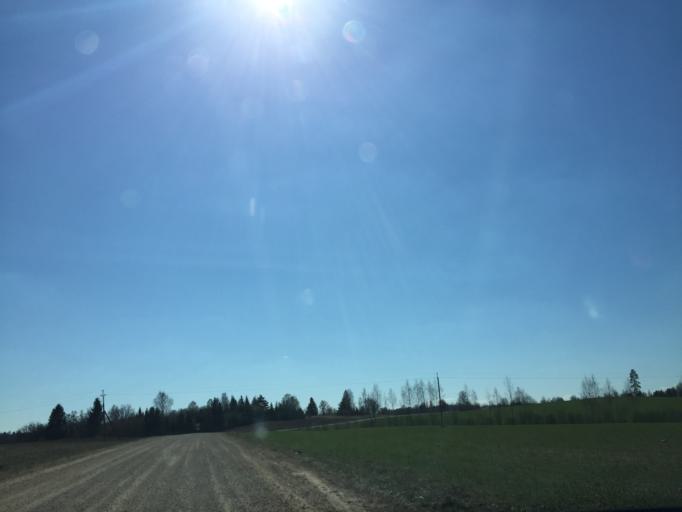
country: EE
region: Viljandimaa
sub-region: Viiratsi vald
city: Viiratsi
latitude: 58.3282
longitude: 25.7069
